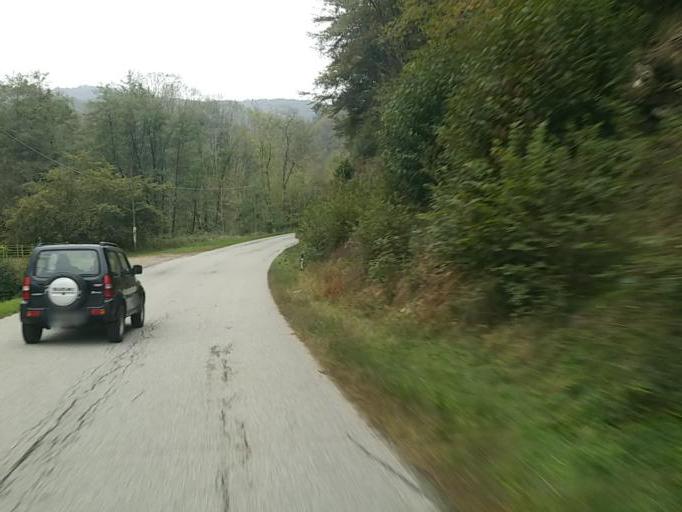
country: IT
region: Piedmont
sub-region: Provincia di Novara
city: Armeno
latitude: 45.8175
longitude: 8.4695
